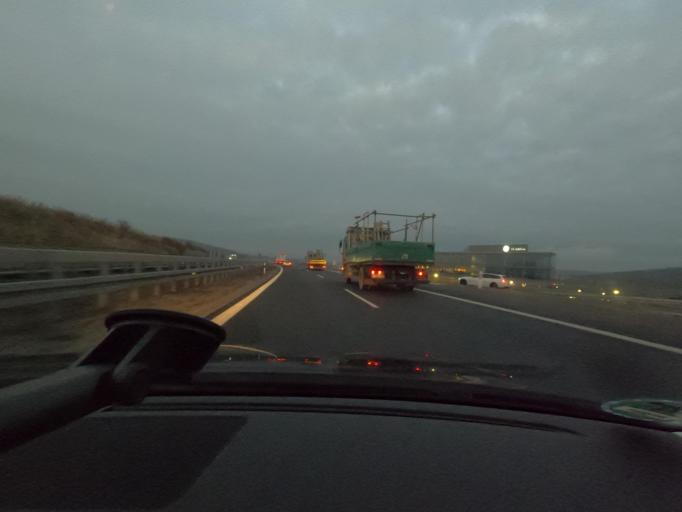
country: DE
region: Bavaria
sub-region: Upper Franconia
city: Lichtenfels
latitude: 50.1283
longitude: 11.0336
